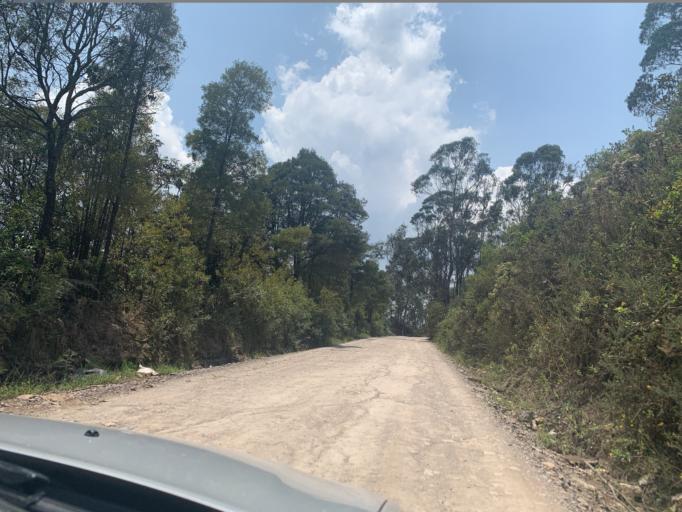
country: CO
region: Boyaca
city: Chiquinquira
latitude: 5.5892
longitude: -73.7519
